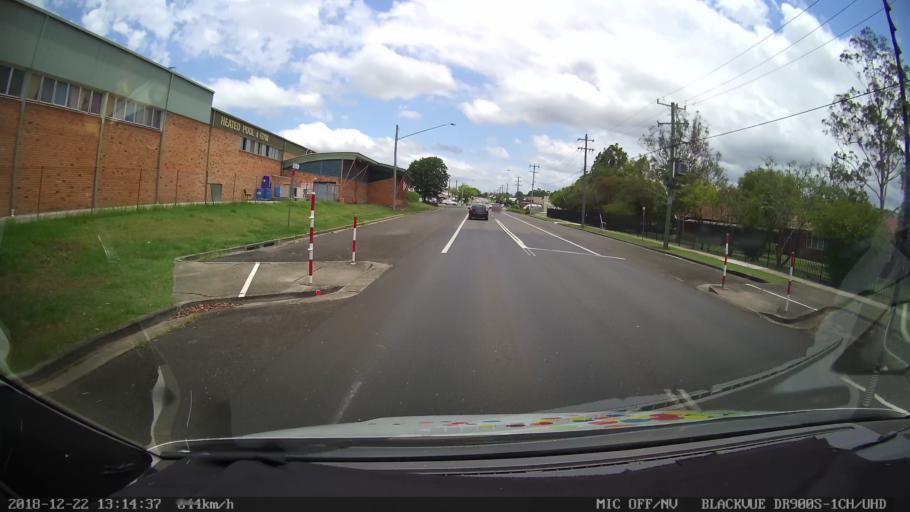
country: AU
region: New South Wales
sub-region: Clarence Valley
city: South Grafton
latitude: -29.7121
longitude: 152.9407
